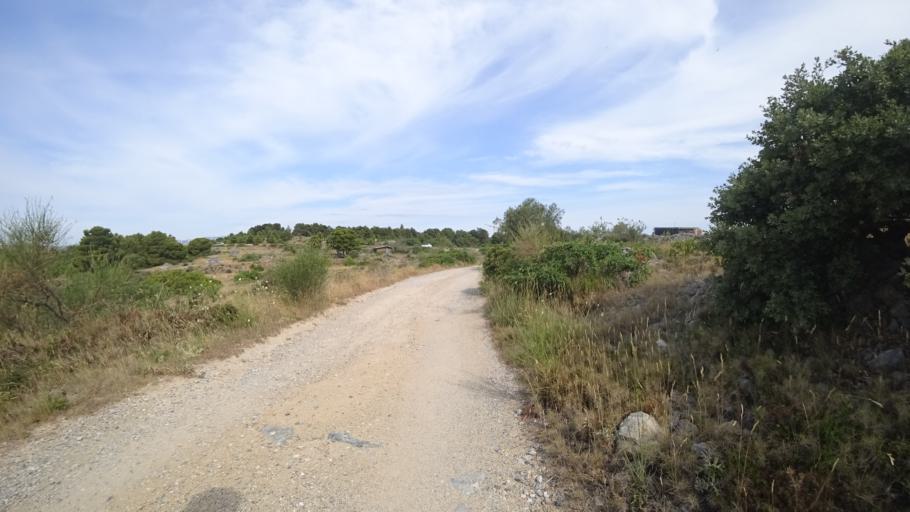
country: FR
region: Languedoc-Roussillon
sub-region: Departement de l'Aude
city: Leucate
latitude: 42.9013
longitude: 3.0321
